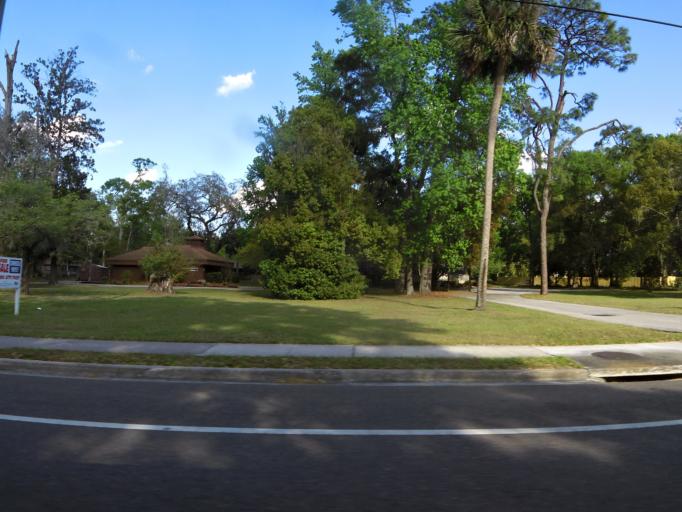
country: US
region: Florida
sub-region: Duval County
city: Jacksonville
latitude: 30.3304
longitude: -81.5969
